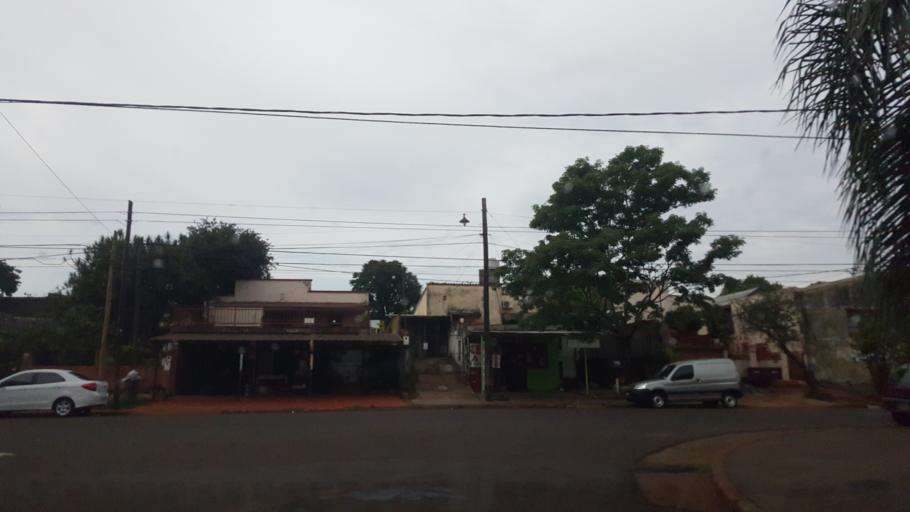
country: AR
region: Misiones
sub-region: Departamento de Capital
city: Posadas
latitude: -27.3884
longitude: -55.8956
